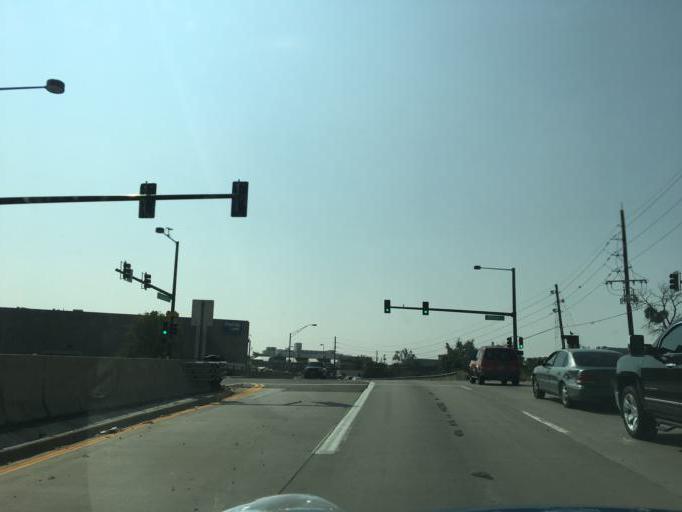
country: US
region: Colorado
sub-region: Denver County
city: Denver
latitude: 39.7761
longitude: -104.9790
